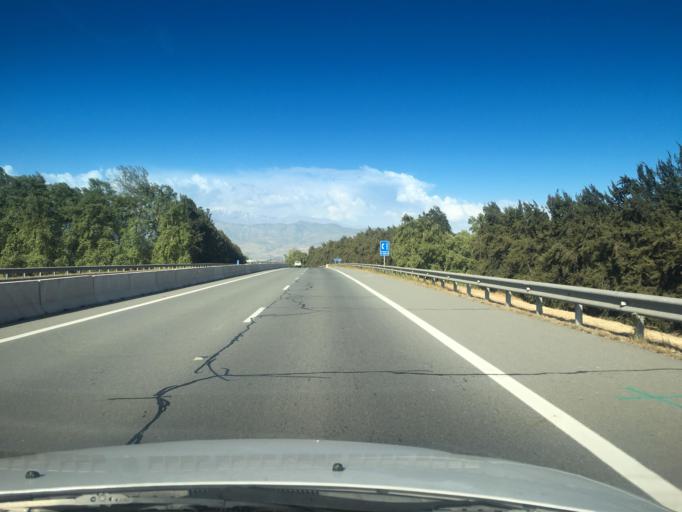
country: CL
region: Santiago Metropolitan
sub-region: Provincia de Chacabuco
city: Chicureo Abajo
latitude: -33.2938
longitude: -70.7134
